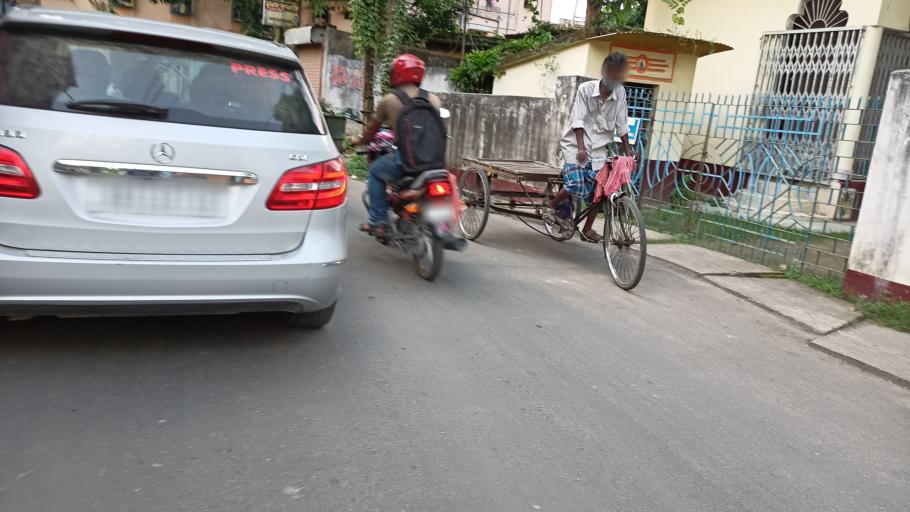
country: IN
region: West Bengal
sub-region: North 24 Parganas
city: Bangaon
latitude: 23.0455
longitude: 88.8258
